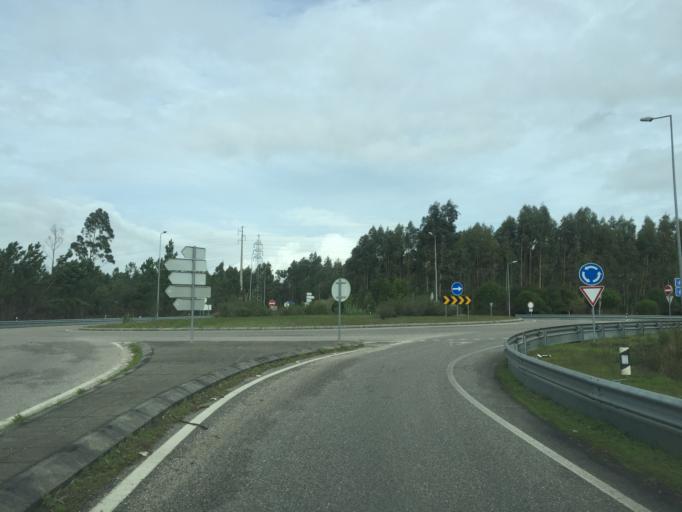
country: PT
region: Coimbra
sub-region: Figueira da Foz
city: Lavos
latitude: 40.0491
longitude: -8.8161
